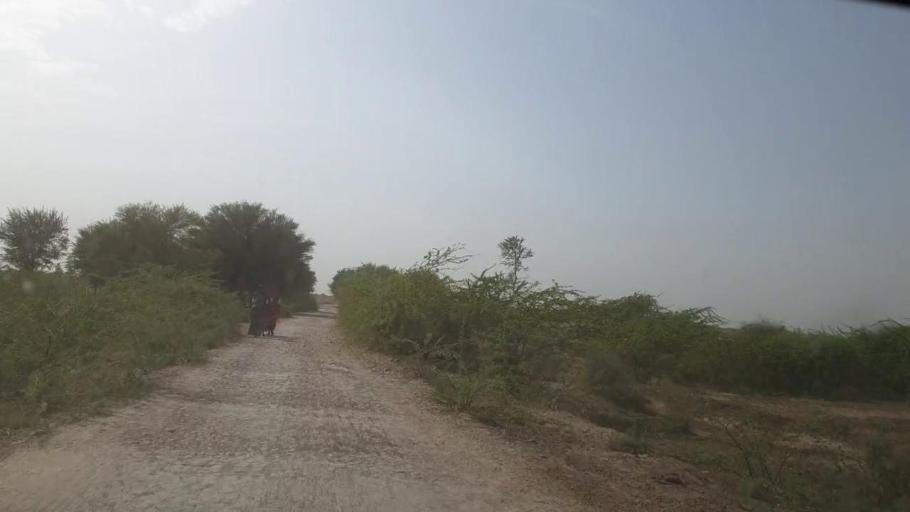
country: PK
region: Sindh
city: Nabisar
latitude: 25.0383
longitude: 69.4996
